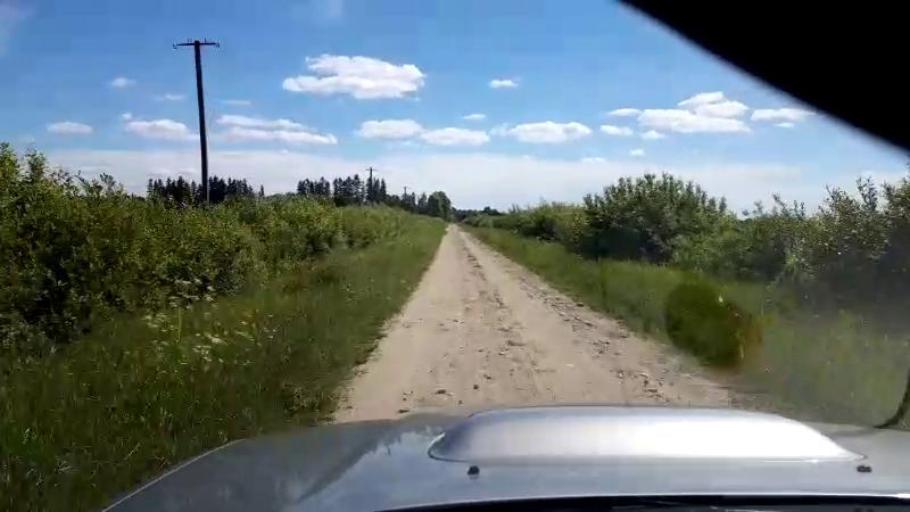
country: EE
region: Paernumaa
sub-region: Halinga vald
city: Parnu-Jaagupi
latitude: 58.5445
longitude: 24.5293
